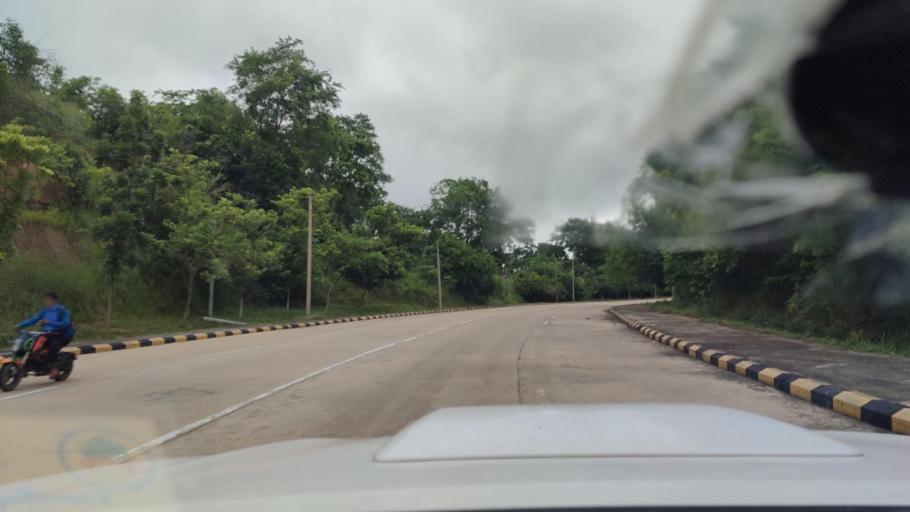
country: MM
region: Mandalay
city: Nay Pyi Taw
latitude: 19.7599
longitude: 96.0708
